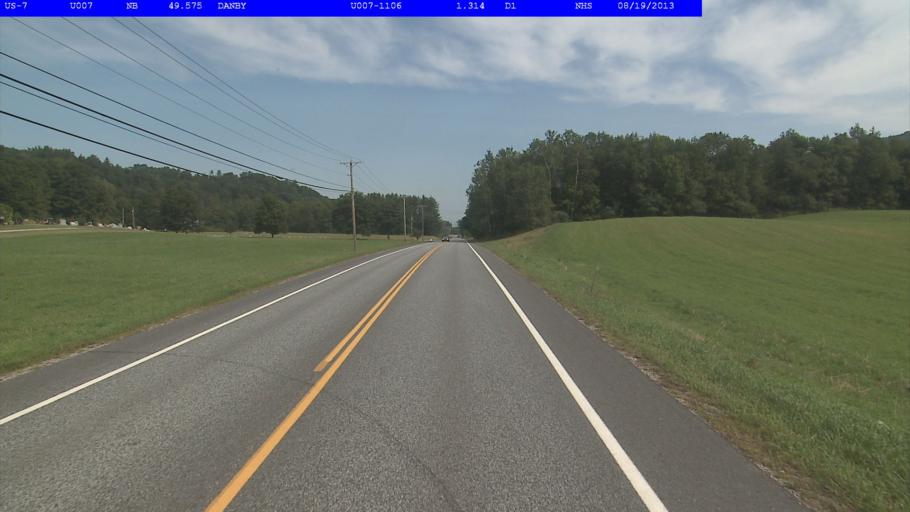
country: US
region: Vermont
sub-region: Bennington County
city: Manchester Center
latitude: 43.3810
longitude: -72.9992
